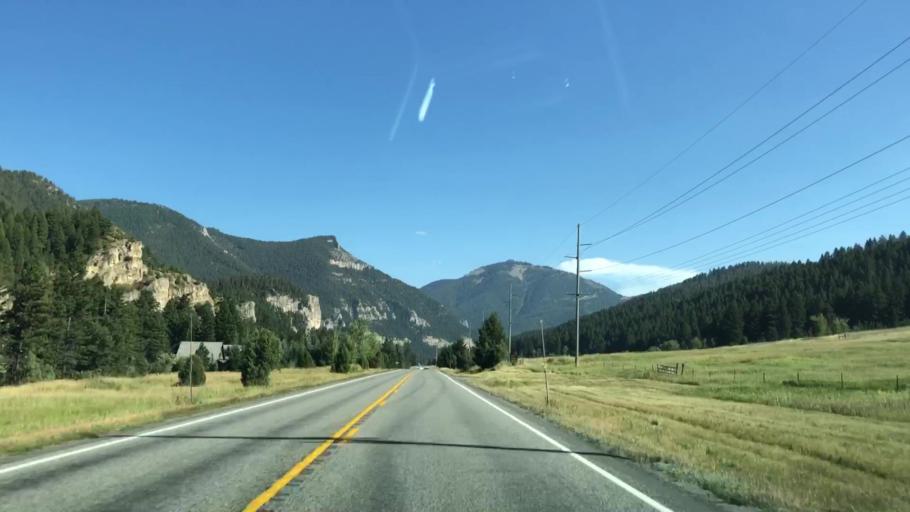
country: US
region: Montana
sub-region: Gallatin County
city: Four Corners
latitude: 45.4698
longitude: -111.2659
